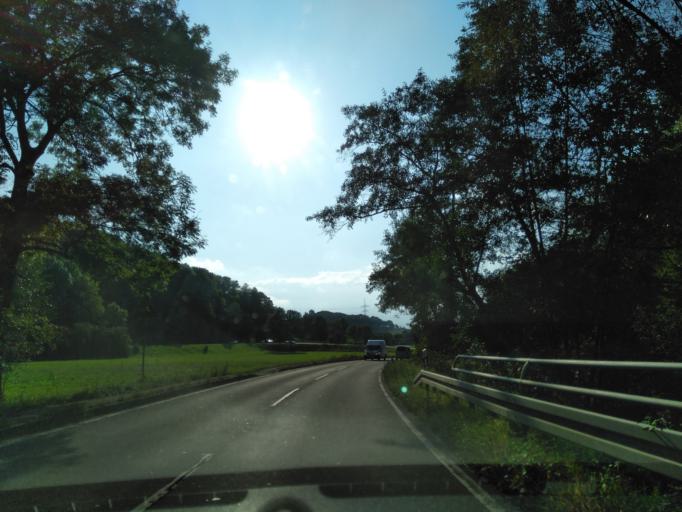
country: DE
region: Baden-Wuerttemberg
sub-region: Regierungsbezirk Stuttgart
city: Oberriexingen
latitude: 48.9232
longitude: 9.0264
